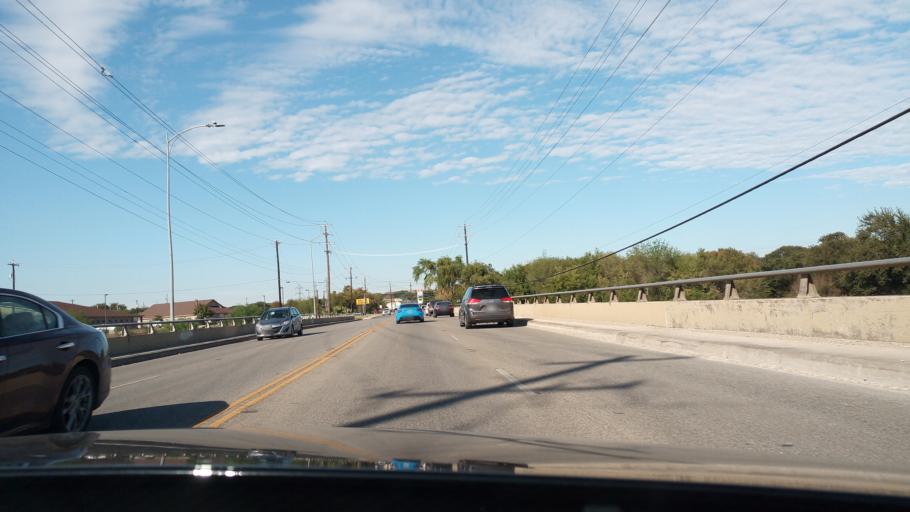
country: US
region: Texas
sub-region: Bexar County
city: Windcrest
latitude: 29.5316
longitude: -98.4301
